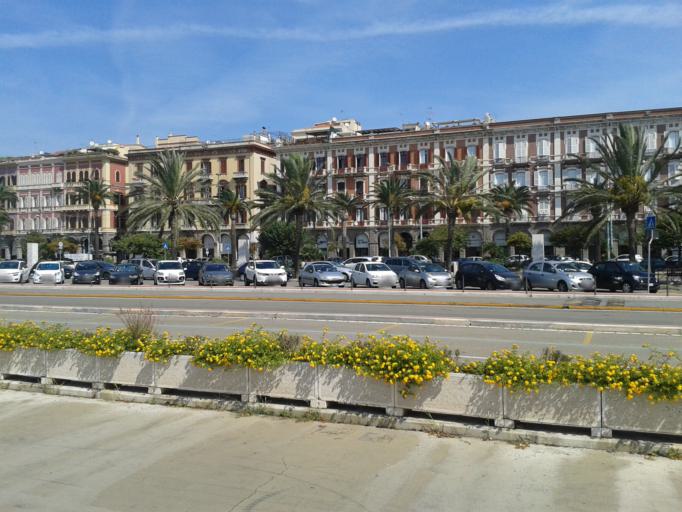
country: IT
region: Sardinia
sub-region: Provincia di Cagliari
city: Cagliari
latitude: 39.2129
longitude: 9.1124
